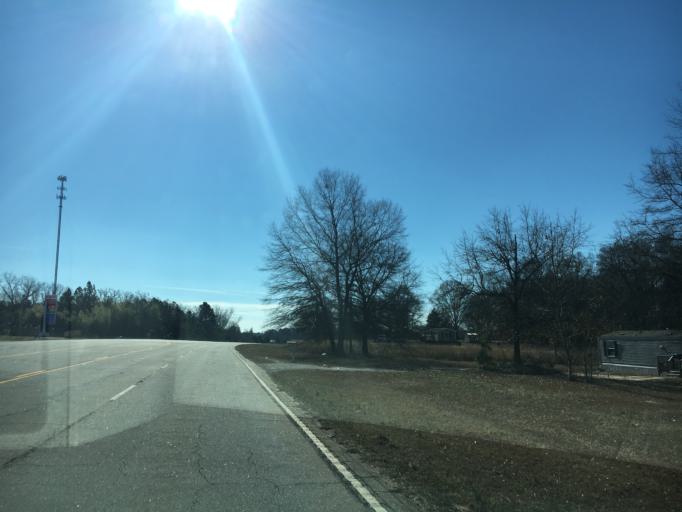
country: US
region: South Carolina
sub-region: Anderson County
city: Homeland Park
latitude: 34.4018
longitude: -82.6877
